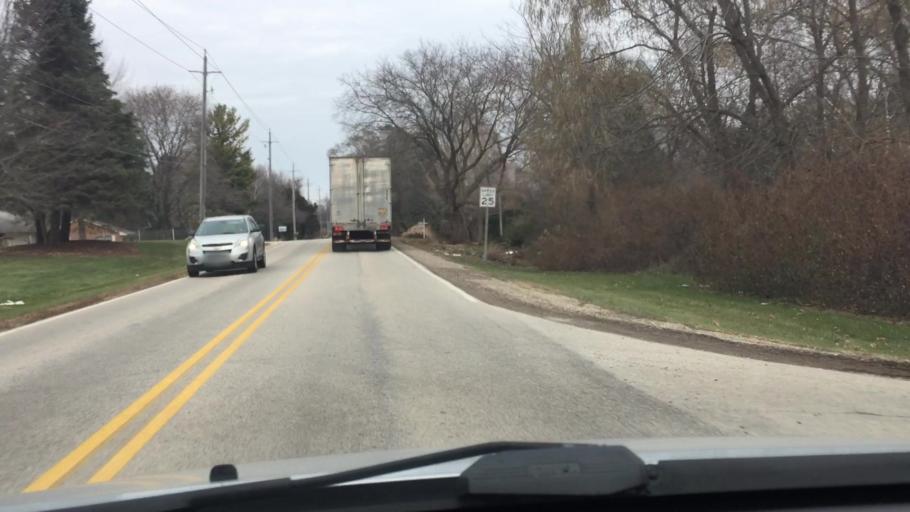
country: US
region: Wisconsin
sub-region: Ozaukee County
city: Cedarburg
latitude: 43.2919
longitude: -87.9640
